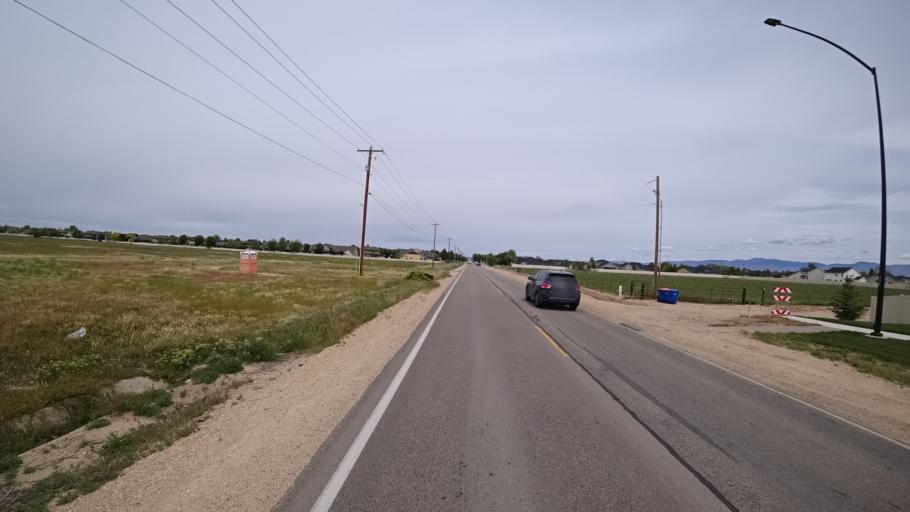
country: US
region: Idaho
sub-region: Ada County
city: Meridian
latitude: 43.5628
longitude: -116.3543
